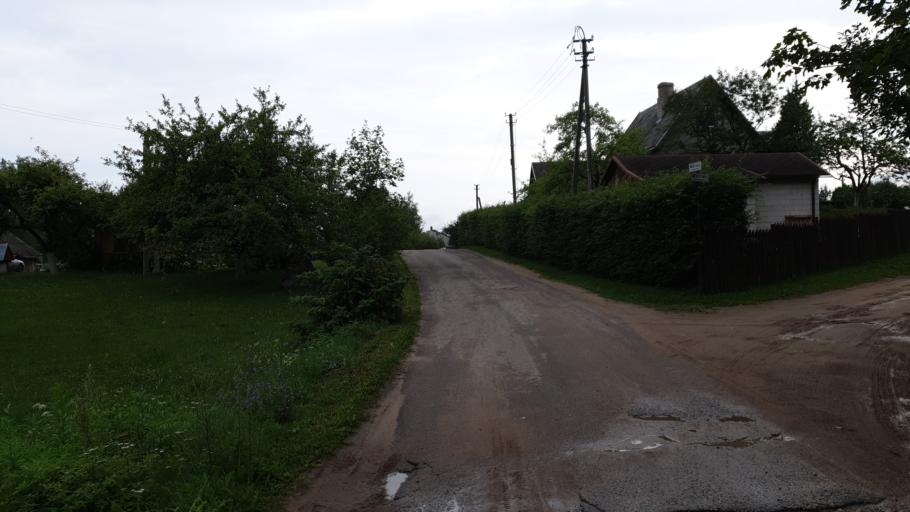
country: LT
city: Grigiskes
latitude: 54.7703
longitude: 25.0172
